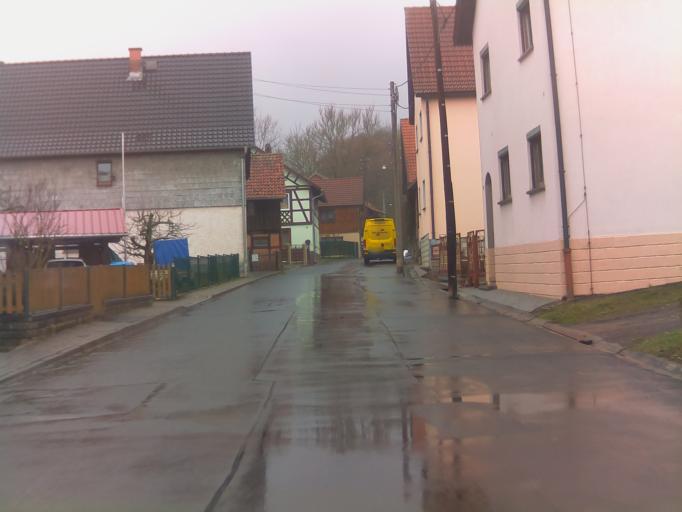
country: DE
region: Thuringia
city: Gleichamberg
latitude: 50.3954
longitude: 10.6254
